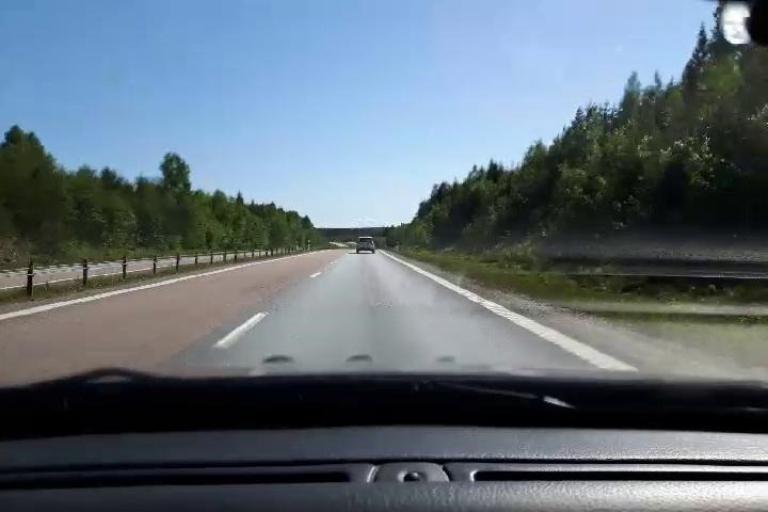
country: SE
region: Gaevleborg
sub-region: Hudiksvalls Kommun
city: Iggesund
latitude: 61.4994
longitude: 16.9855
